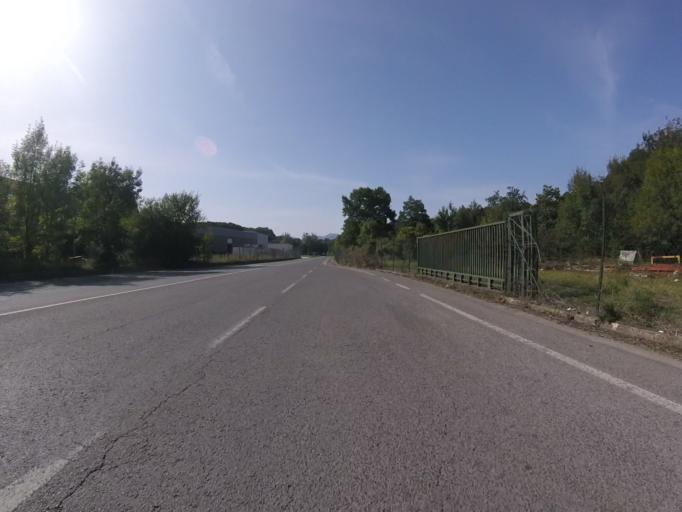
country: ES
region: Navarre
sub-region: Provincia de Navarra
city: Zugarramurdi
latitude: 43.1799
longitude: -1.4909
